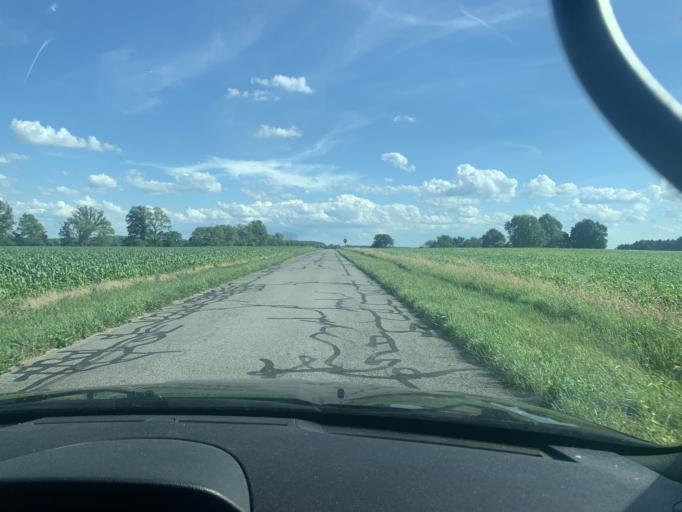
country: US
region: Ohio
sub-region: Logan County
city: De Graff
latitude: 40.3269
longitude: -83.8729
